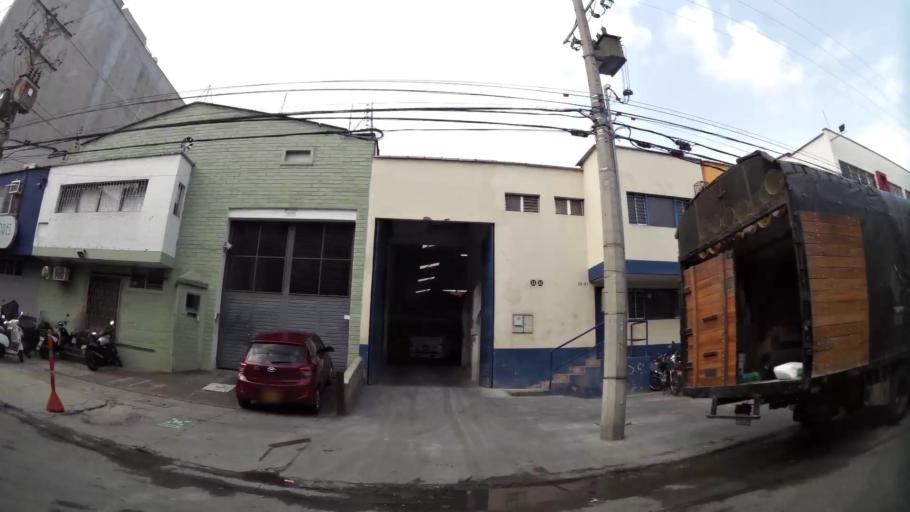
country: CO
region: Antioquia
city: Itagui
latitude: 6.2167
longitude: -75.5828
